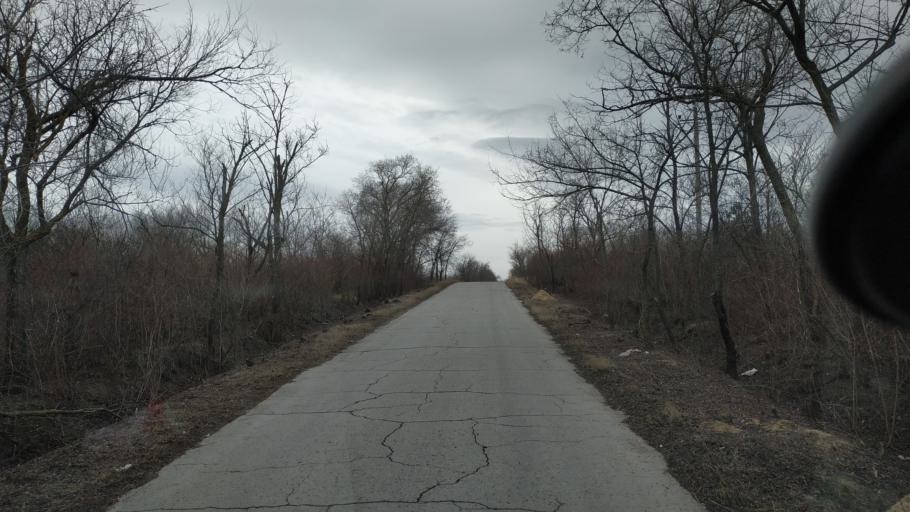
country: MD
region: Telenesti
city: Cocieri
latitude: 47.3320
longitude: 29.0875
